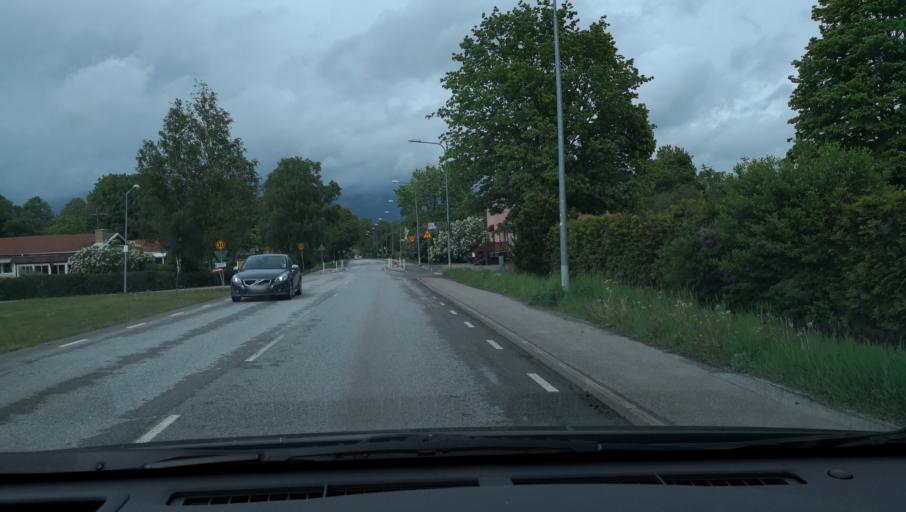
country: SE
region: Uppsala
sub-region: Enkopings Kommun
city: Orsundsbro
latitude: 59.7327
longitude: 17.3070
